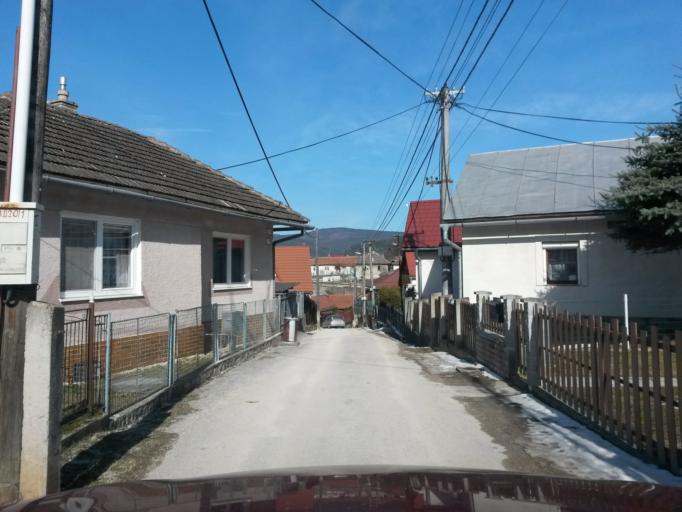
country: SK
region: Kosicky
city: Gelnica
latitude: 48.8720
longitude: 20.9914
